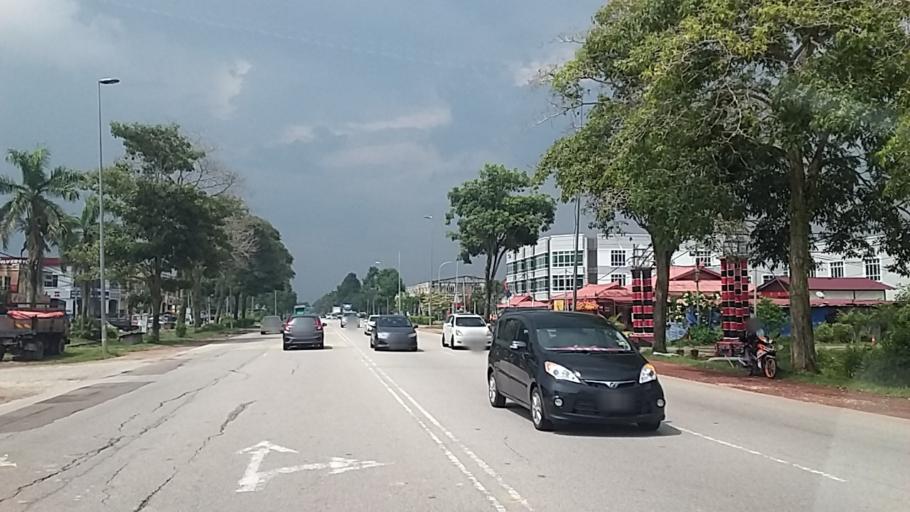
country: MY
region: Johor
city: Parit Raja
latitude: 1.8674
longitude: 103.1187
